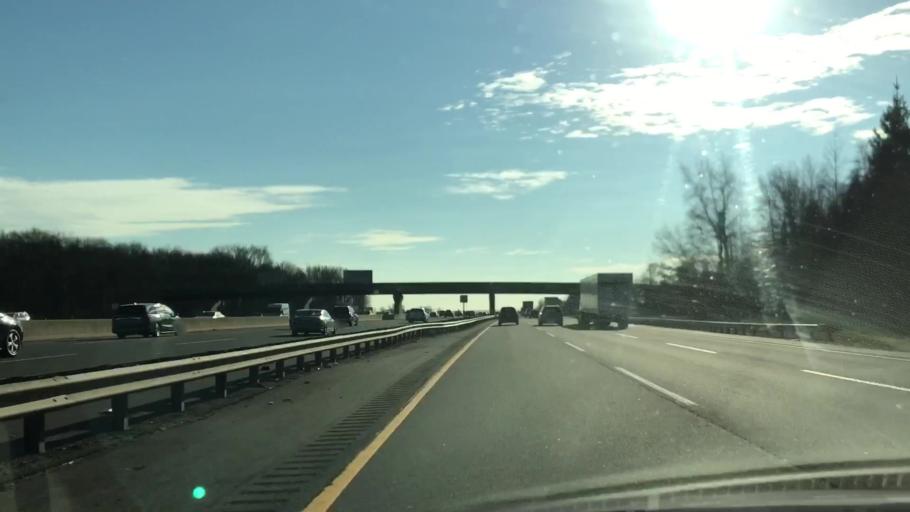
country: US
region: New Jersey
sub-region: Middlesex County
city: Helmetta
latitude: 40.4019
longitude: -74.4525
